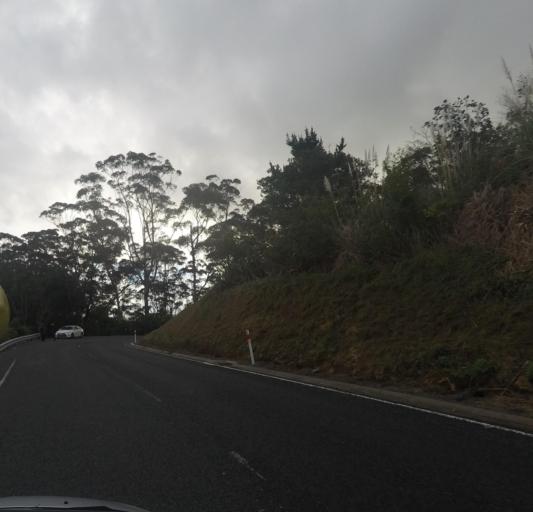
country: NZ
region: Auckland
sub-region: Auckland
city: Warkworth
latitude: -36.3762
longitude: 174.8061
